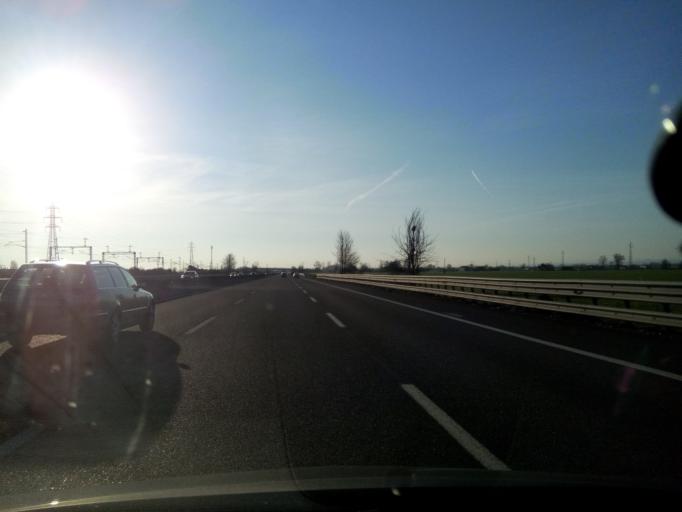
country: IT
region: Emilia-Romagna
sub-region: Provincia di Piacenza
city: Pontenure
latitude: 44.9958
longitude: 9.8256
